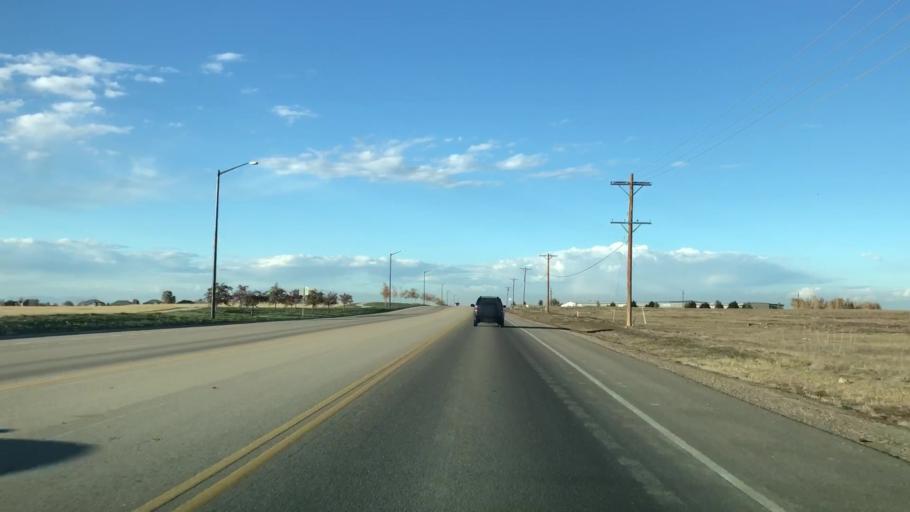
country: US
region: Colorado
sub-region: Larimer County
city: Loveland
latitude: 40.4364
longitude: -105.0204
